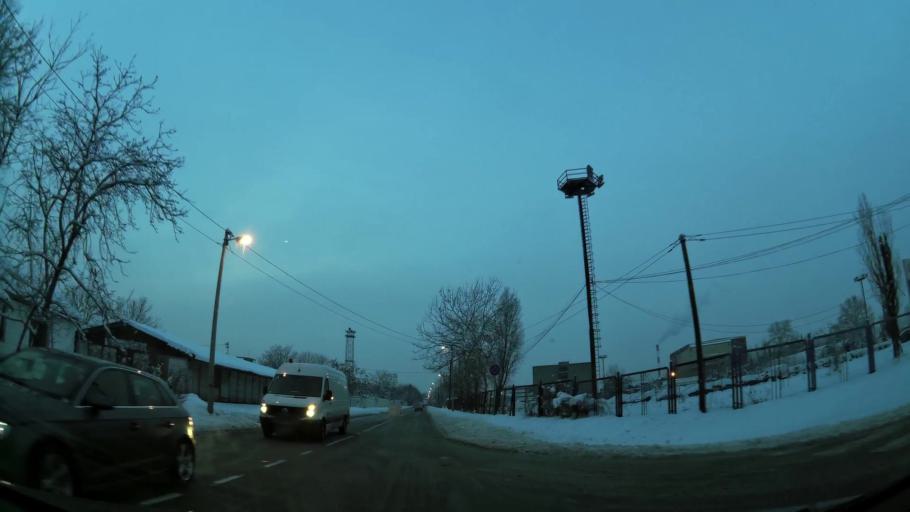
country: RS
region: Central Serbia
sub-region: Belgrade
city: Stari Grad
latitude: 44.8214
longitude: 20.4839
